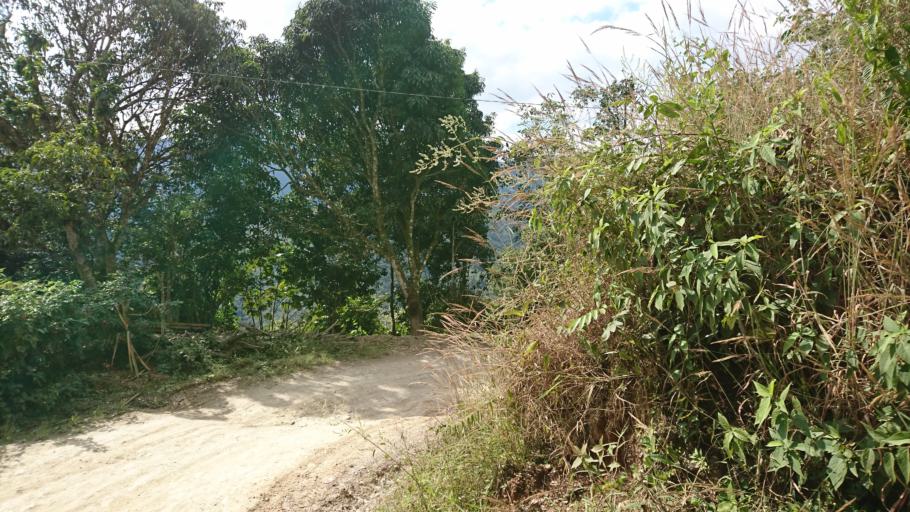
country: BO
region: La Paz
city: Coroico
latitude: -16.0872
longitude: -67.7859
